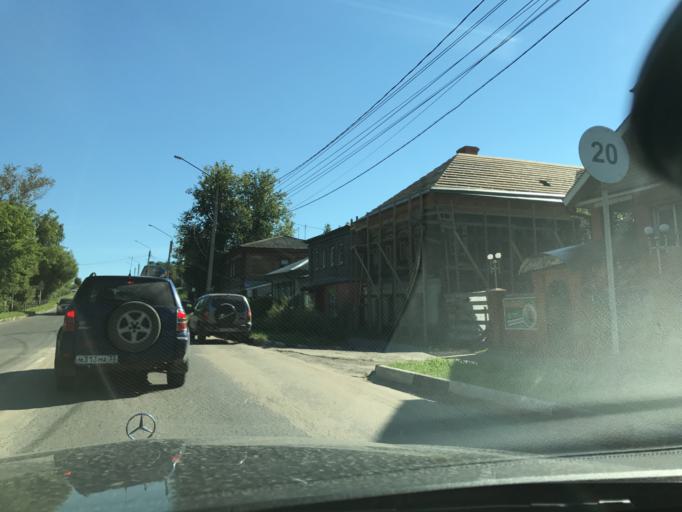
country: RU
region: Vladimir
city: Kirzhach
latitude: 56.1596
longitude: 38.8681
